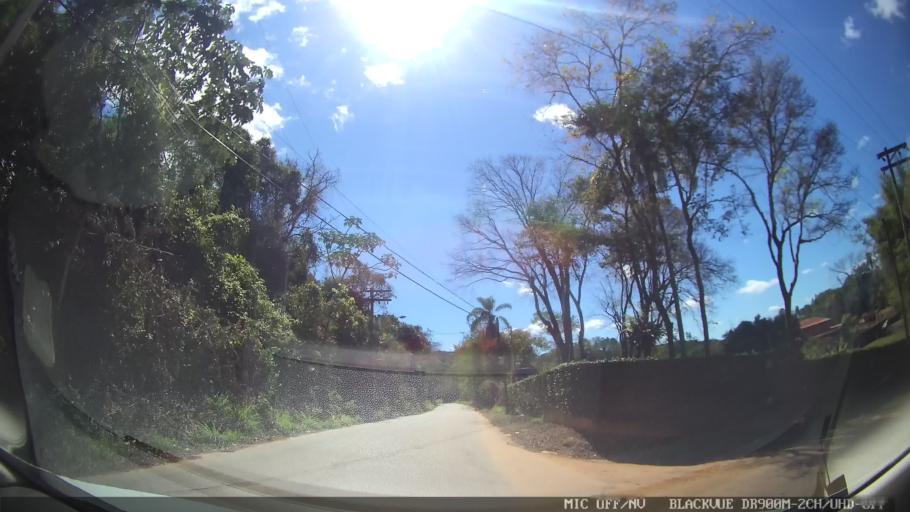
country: BR
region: Sao Paulo
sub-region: Jarinu
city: Jarinu
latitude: -23.1649
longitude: -46.7342
